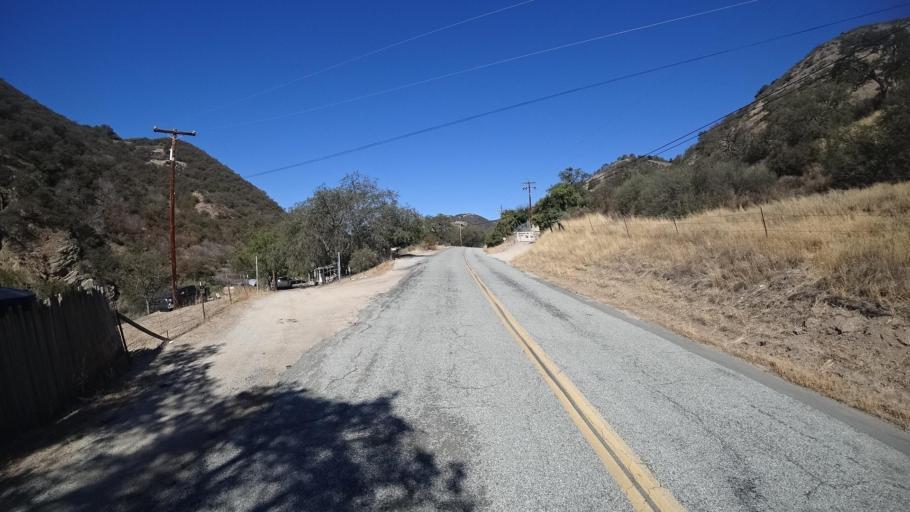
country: US
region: California
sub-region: Monterey County
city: Soledad
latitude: 36.2602
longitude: -121.4274
